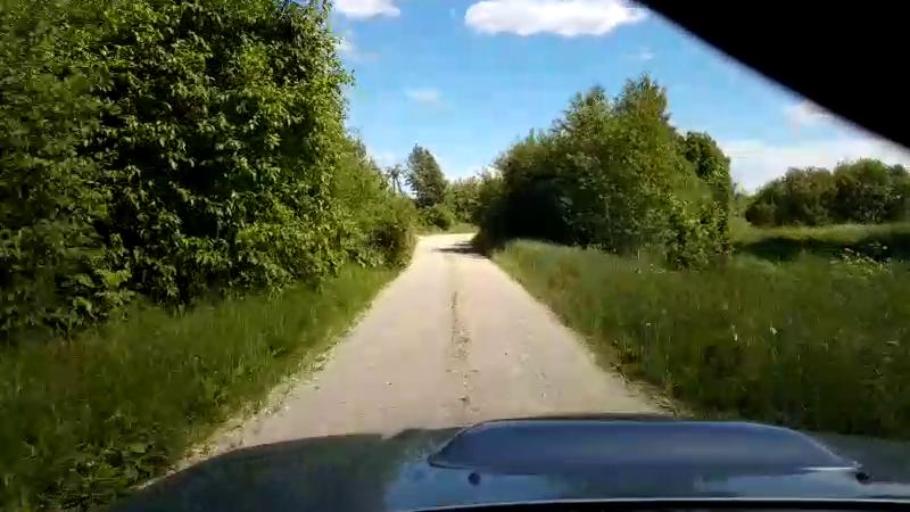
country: EE
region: Paernumaa
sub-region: Halinga vald
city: Parnu-Jaagupi
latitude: 58.5223
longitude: 24.5207
